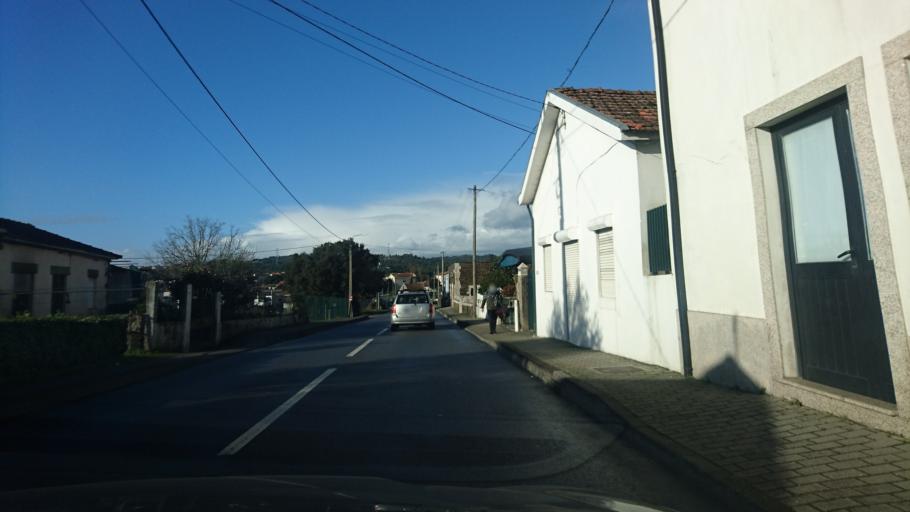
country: PT
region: Porto
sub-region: Paredes
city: Recarei
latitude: 41.1518
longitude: -8.4083
